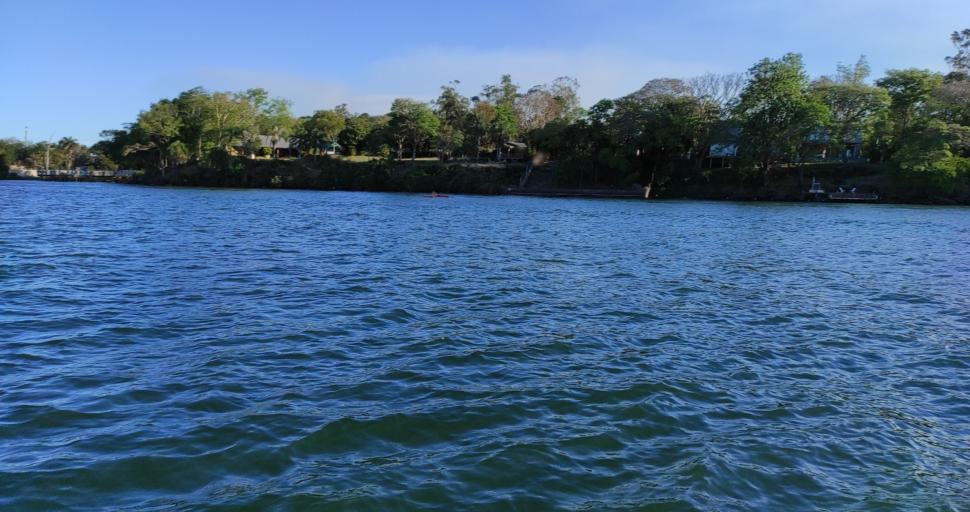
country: AR
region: Misiones
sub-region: Departamento de Capital
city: Posadas
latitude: -27.3520
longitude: -55.9319
